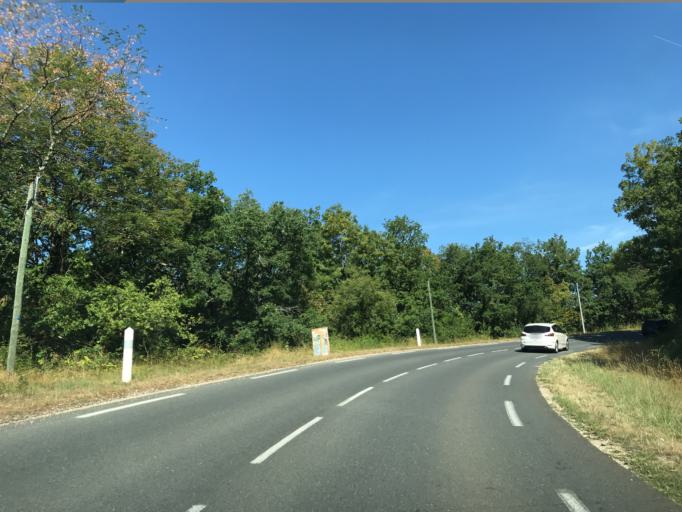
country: FR
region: Limousin
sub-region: Departement de la Correze
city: Larche
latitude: 45.0814
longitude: 1.3737
